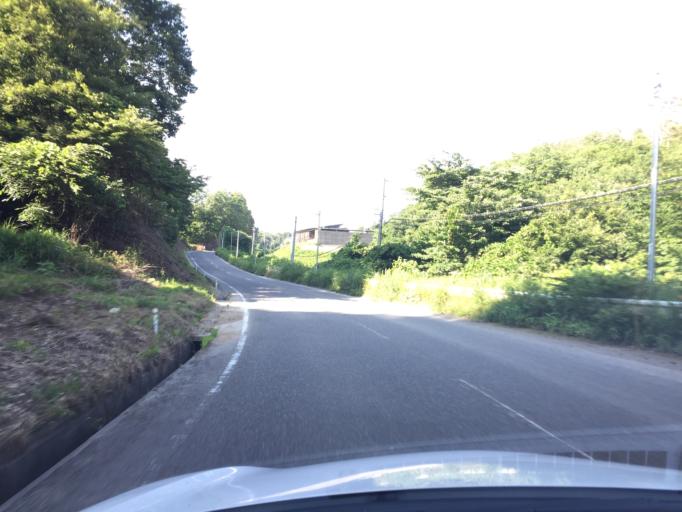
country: JP
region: Fukushima
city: Ishikawa
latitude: 37.2073
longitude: 140.4825
